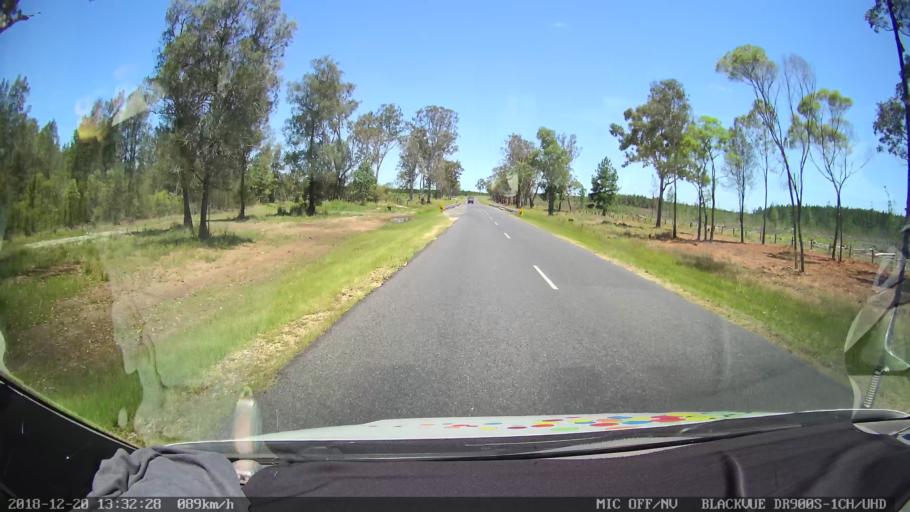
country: AU
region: New South Wales
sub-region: Clarence Valley
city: Gordon
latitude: -29.2321
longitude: 152.9890
